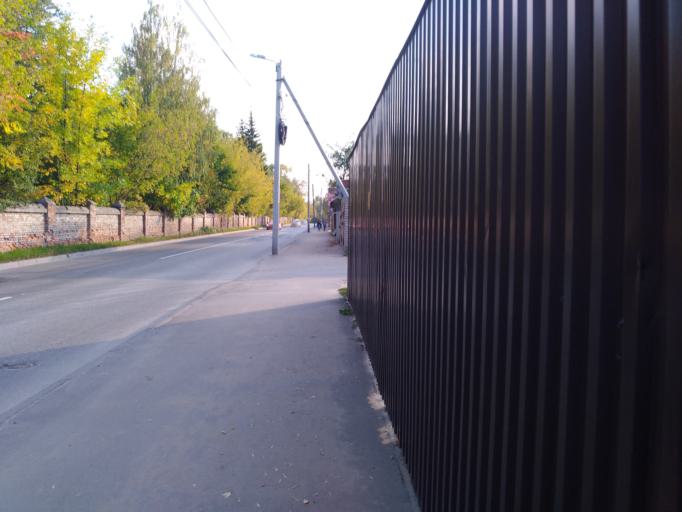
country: RU
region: Kaluga
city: Kaluga
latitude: 54.5250
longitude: 36.2535
